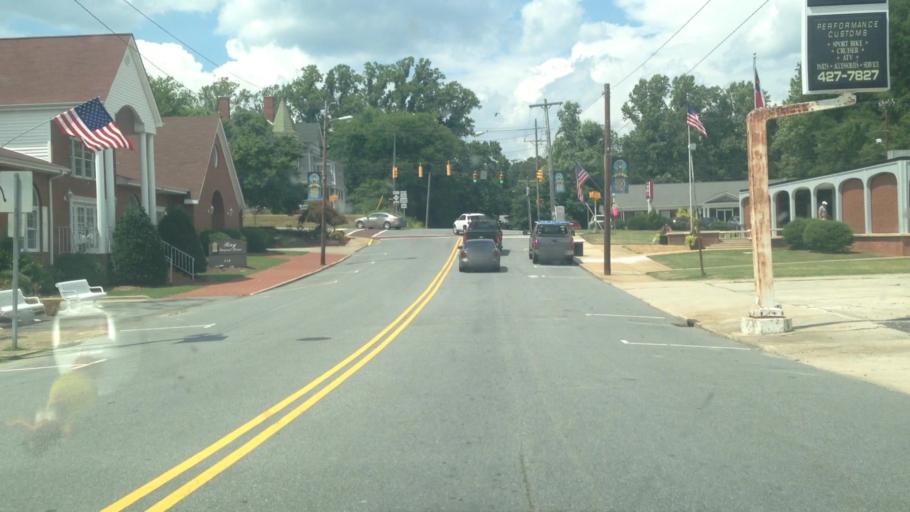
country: US
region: North Carolina
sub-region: Rockingham County
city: Madison
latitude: 36.3880
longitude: -79.9596
